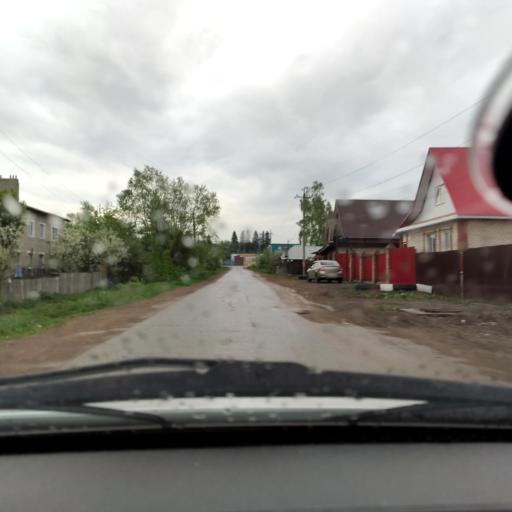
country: RU
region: Bashkortostan
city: Iglino
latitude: 54.8304
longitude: 56.4102
